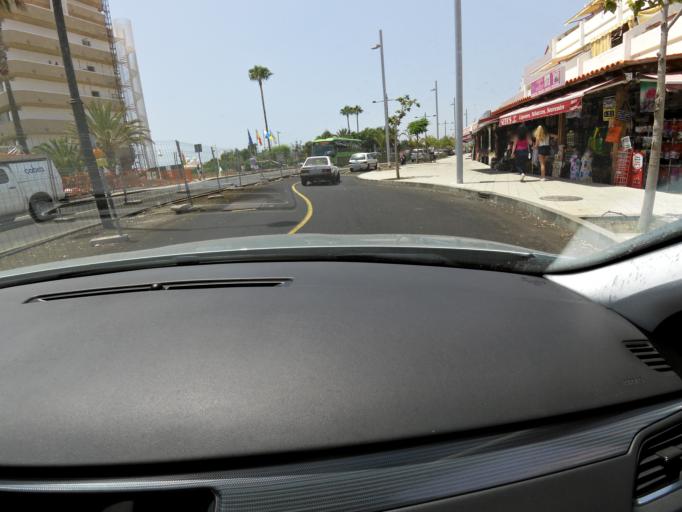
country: ES
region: Canary Islands
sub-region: Provincia de Santa Cruz de Tenerife
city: Playa de las Americas
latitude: 28.0747
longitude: -16.7312
